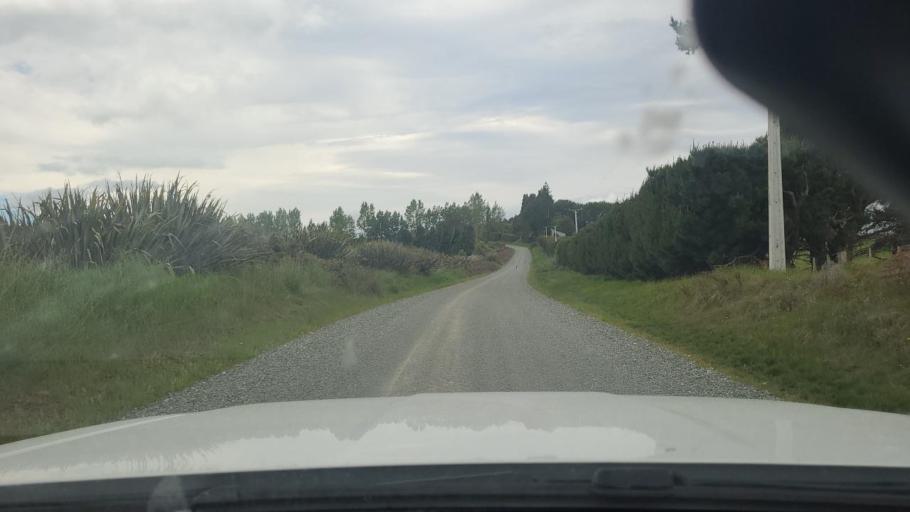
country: NZ
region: Southland
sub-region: Southland District
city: Te Anau
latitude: -45.5677
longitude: 167.7731
